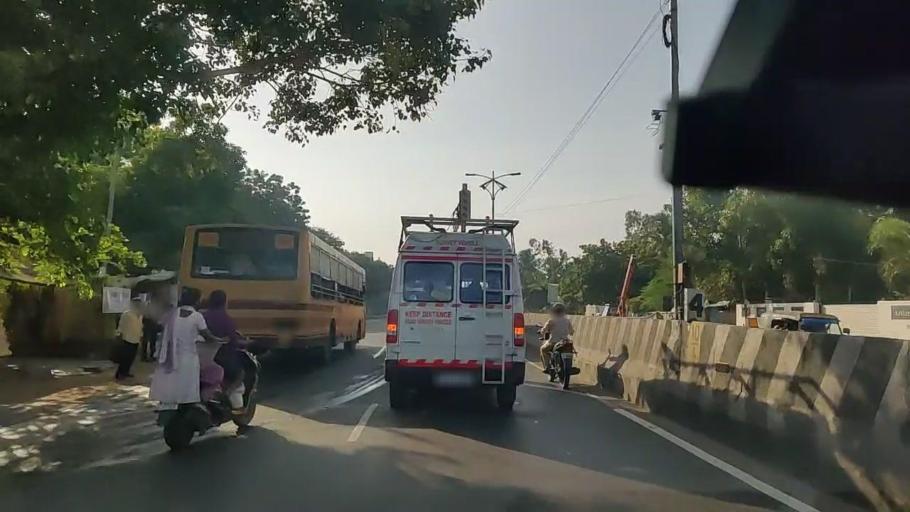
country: IN
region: Tamil Nadu
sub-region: Thiruvallur
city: Chinnasekkadu
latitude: 13.1390
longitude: 80.2278
